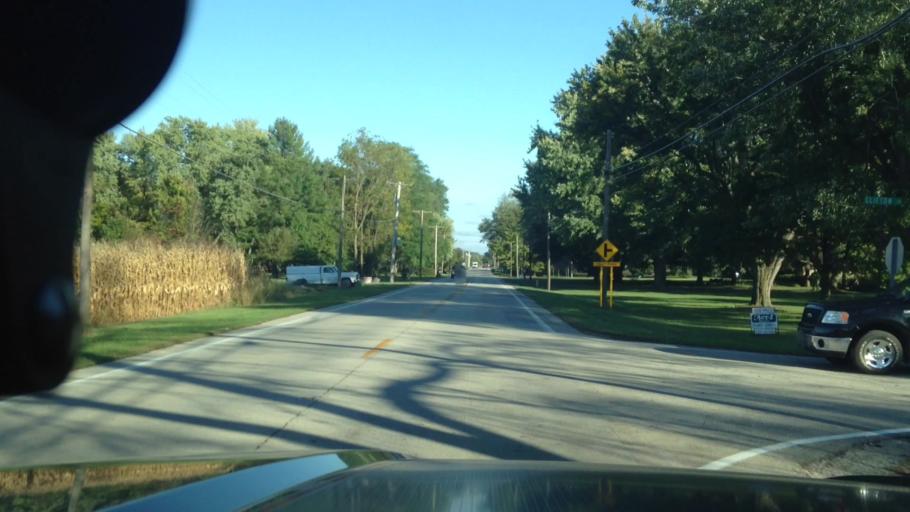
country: US
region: Ohio
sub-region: Darke County
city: Greenville
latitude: 40.1133
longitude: -84.6627
